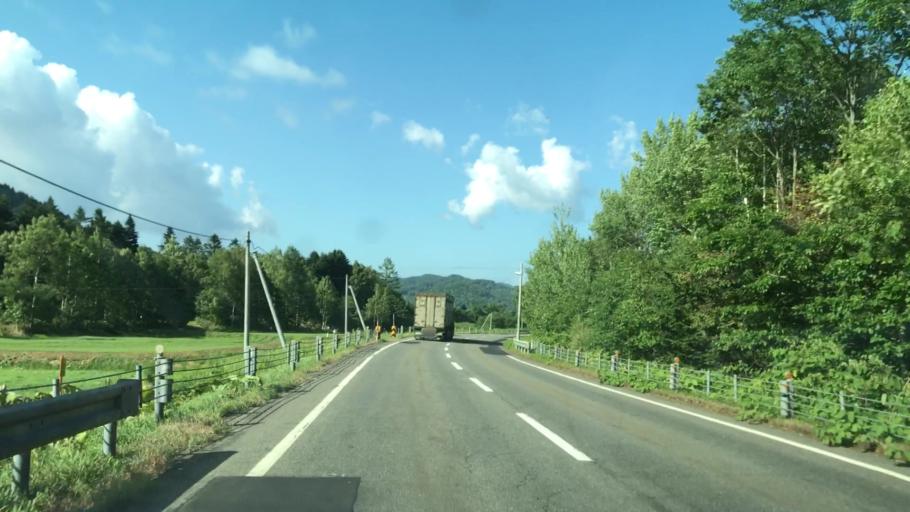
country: JP
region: Hokkaido
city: Shimo-furano
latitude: 42.8650
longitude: 142.4237
